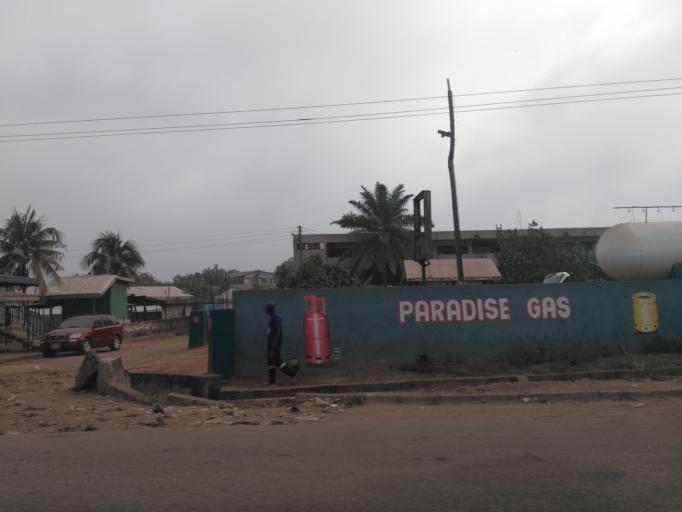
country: GH
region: Ashanti
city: Tafo
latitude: 6.7115
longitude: -1.5998
